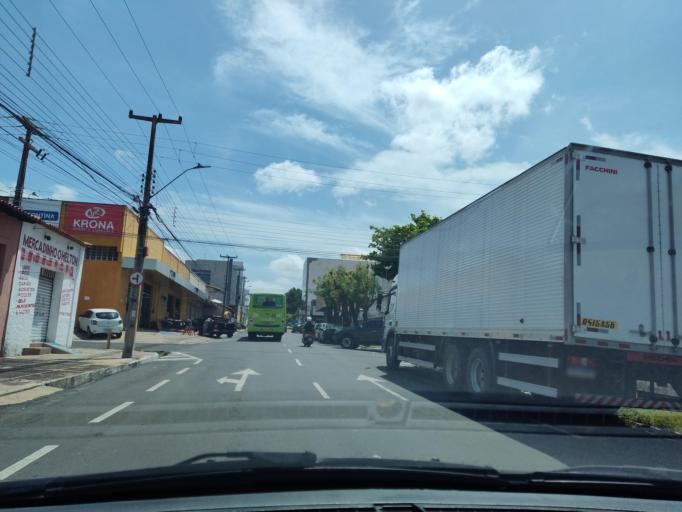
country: BR
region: Piaui
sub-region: Teresina
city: Teresina
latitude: -5.0863
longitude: -42.8197
